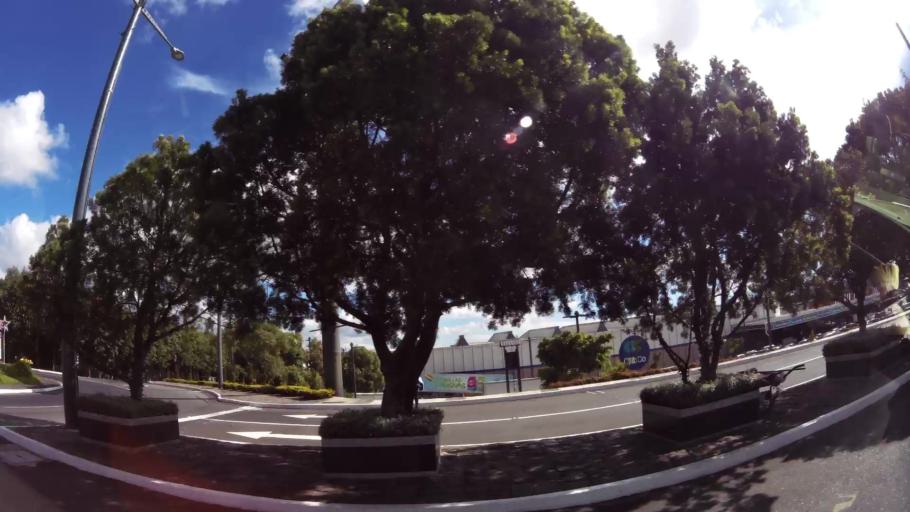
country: GT
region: Guatemala
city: Mixco
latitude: 14.6224
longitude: -90.5605
